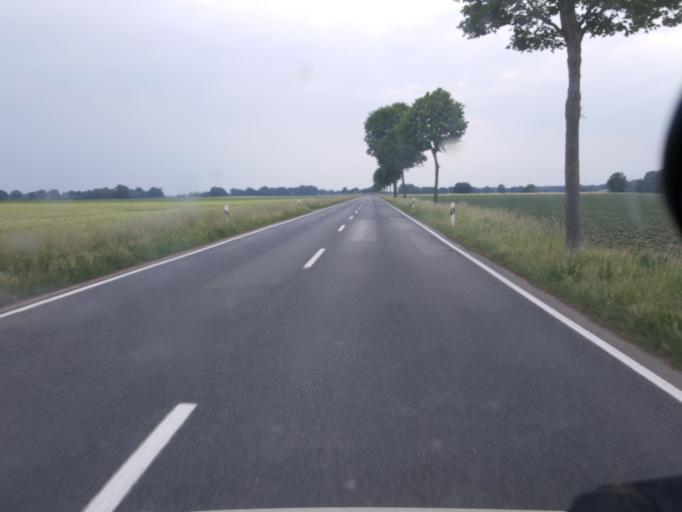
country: DE
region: Lower Saxony
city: Stolzenau
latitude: 52.5055
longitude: 9.0578
